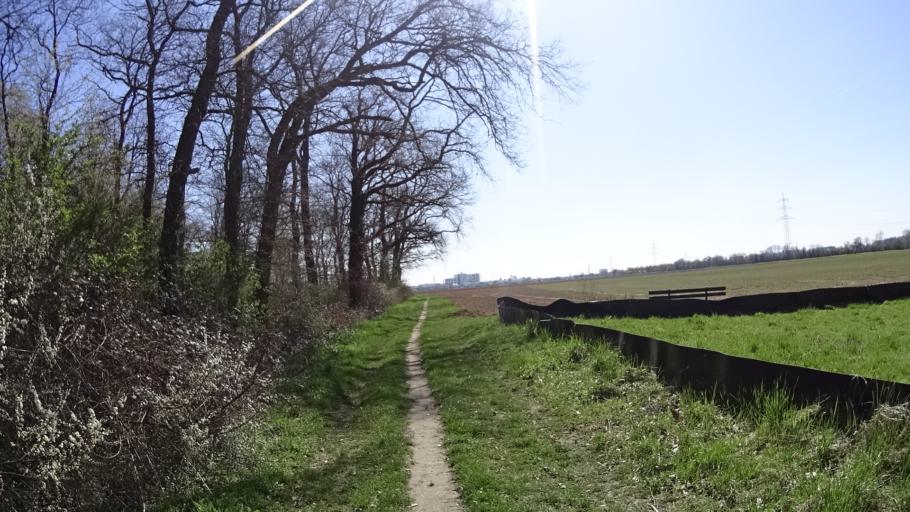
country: DE
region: Baden-Wuerttemberg
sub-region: Karlsruhe Region
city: Plankstadt
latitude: 49.4155
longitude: 8.5736
